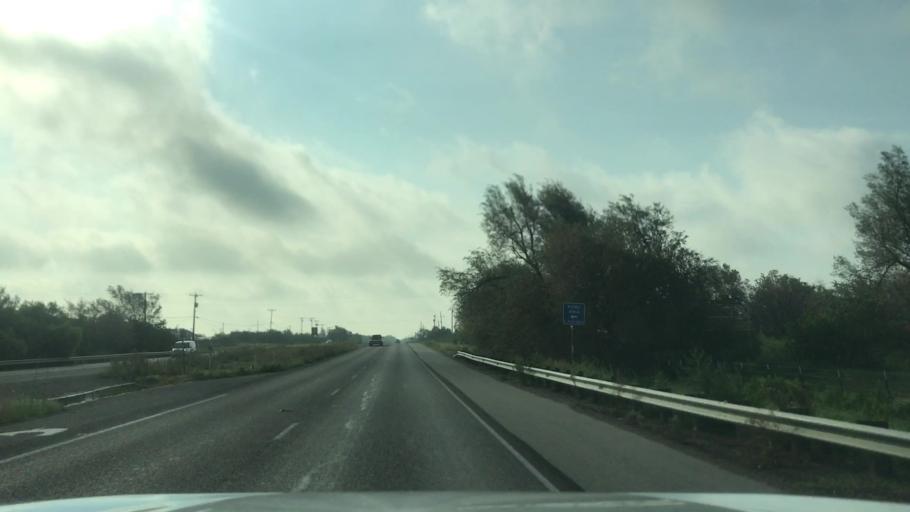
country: US
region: Texas
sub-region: Garza County
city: Post
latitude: 33.2054
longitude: -101.3956
